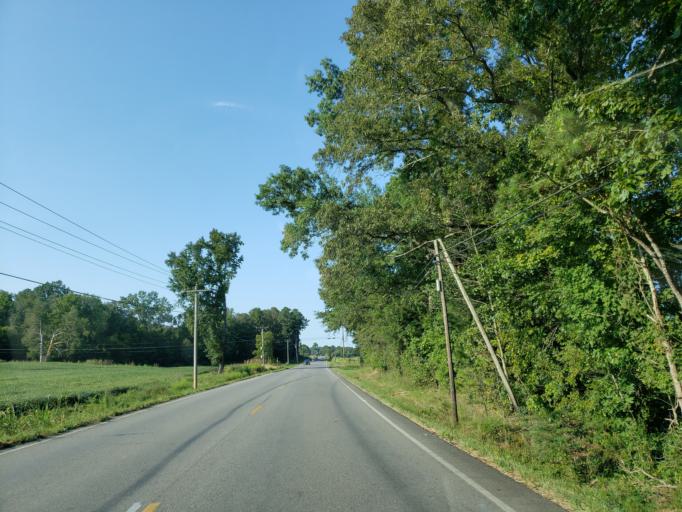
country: US
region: Tennessee
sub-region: Bradley County
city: Wildwood Lake
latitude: 35.0130
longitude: -84.7337
